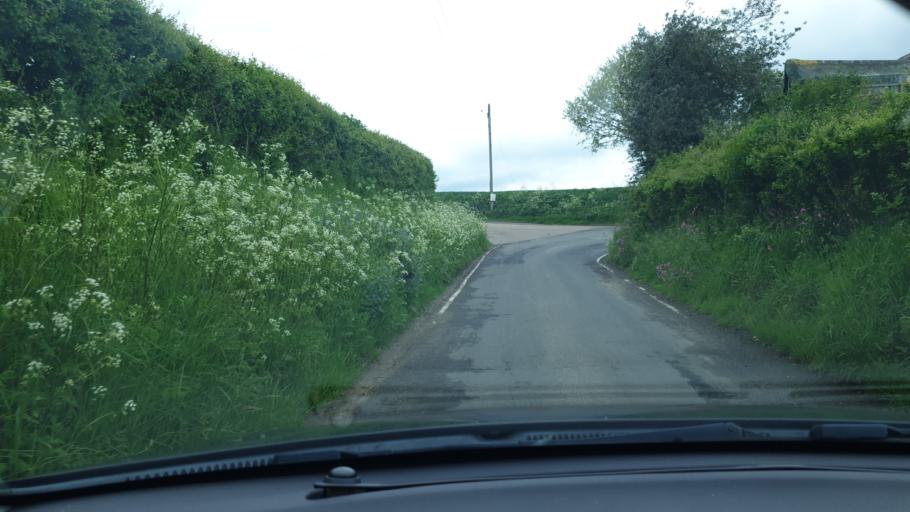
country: GB
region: England
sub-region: Essex
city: Dovercourt
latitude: 51.9138
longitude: 1.1998
